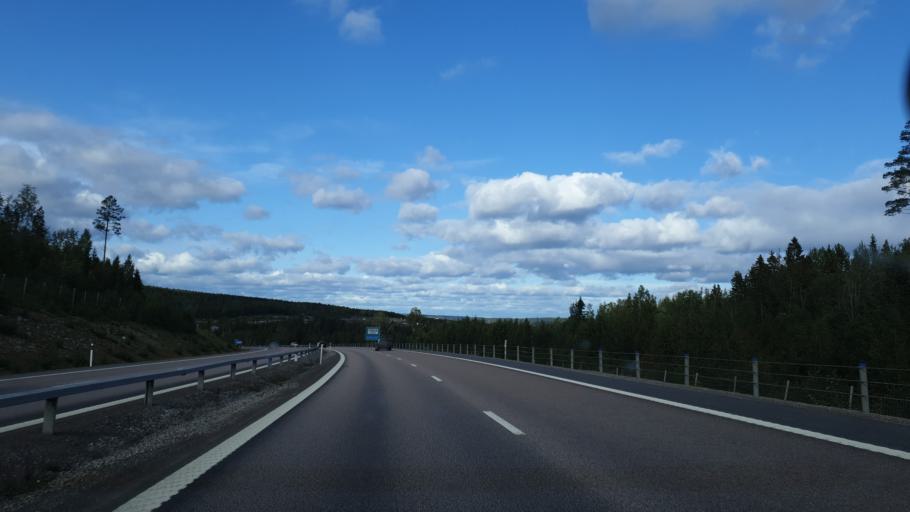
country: SE
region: Vaesternorrland
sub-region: Sundsvalls Kommun
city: Stockvik
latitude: 62.3268
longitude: 17.3452
